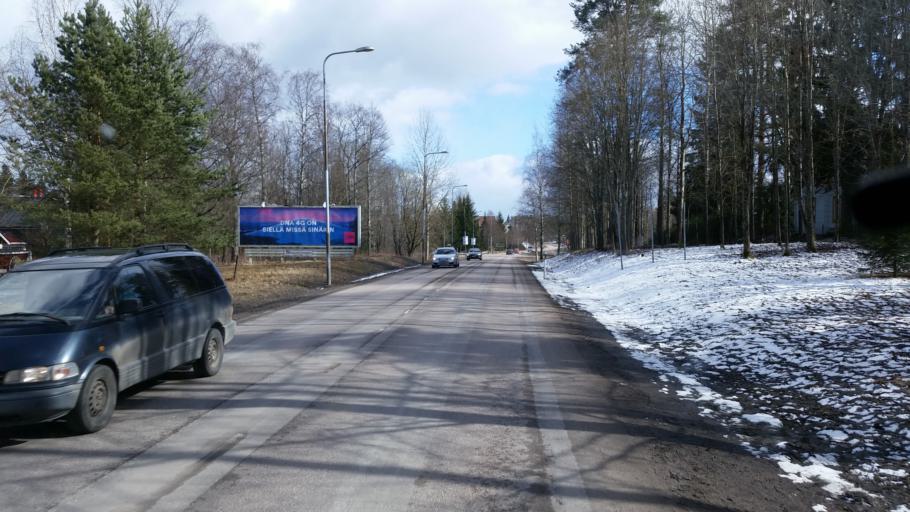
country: FI
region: South Karelia
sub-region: Imatra
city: Imatra
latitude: 61.1711
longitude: 28.7555
